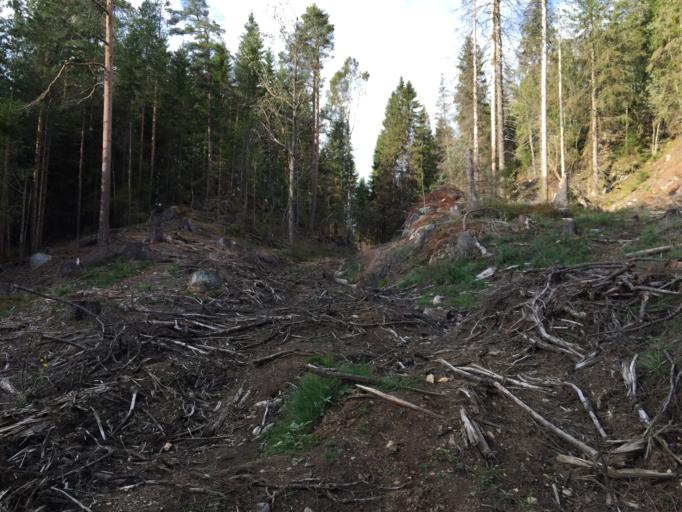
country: NO
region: Akershus
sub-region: Raelingen
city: Fjerdingby
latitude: 59.9204
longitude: 11.0317
